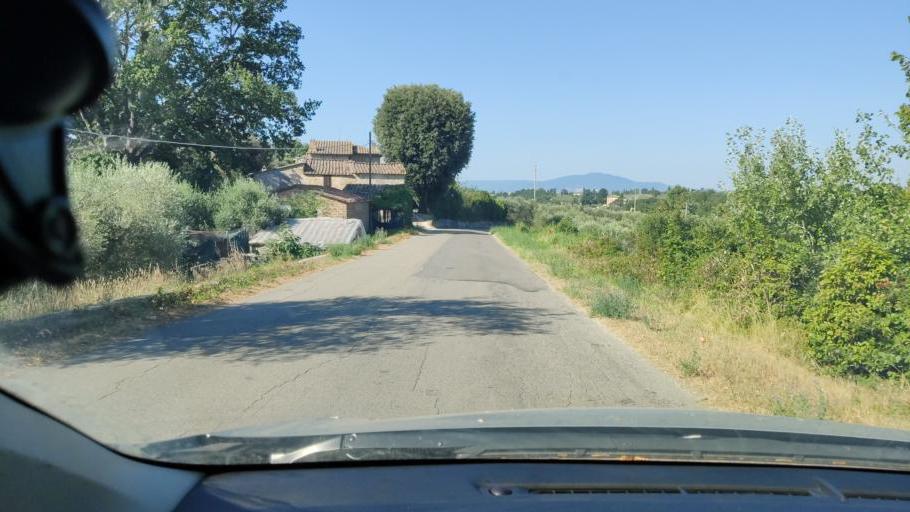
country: IT
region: Umbria
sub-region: Provincia di Terni
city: Fornole
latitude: 42.5296
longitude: 12.4466
